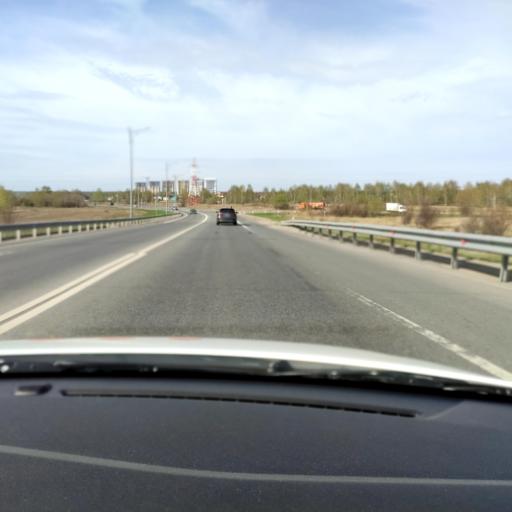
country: RU
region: Tatarstan
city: Stolbishchi
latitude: 55.6963
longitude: 49.2240
